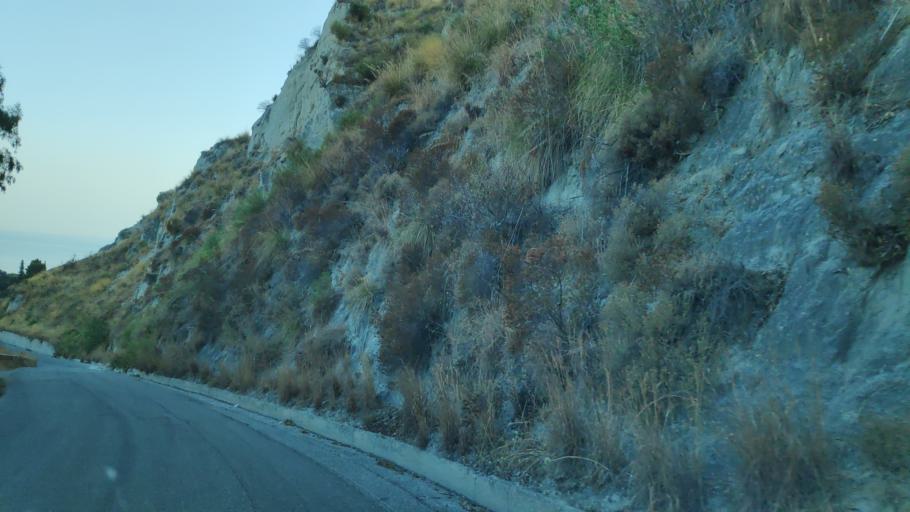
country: IT
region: Calabria
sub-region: Provincia di Reggio Calabria
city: Bova Marina
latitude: 37.9506
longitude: 15.9204
